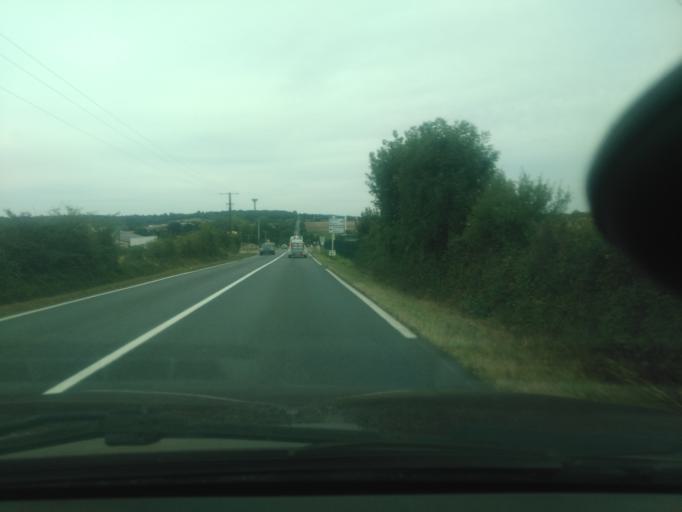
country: FR
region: Pays de la Loire
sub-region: Departement de la Vendee
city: Bazoges-en-Pareds
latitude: 46.6782
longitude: -0.9192
